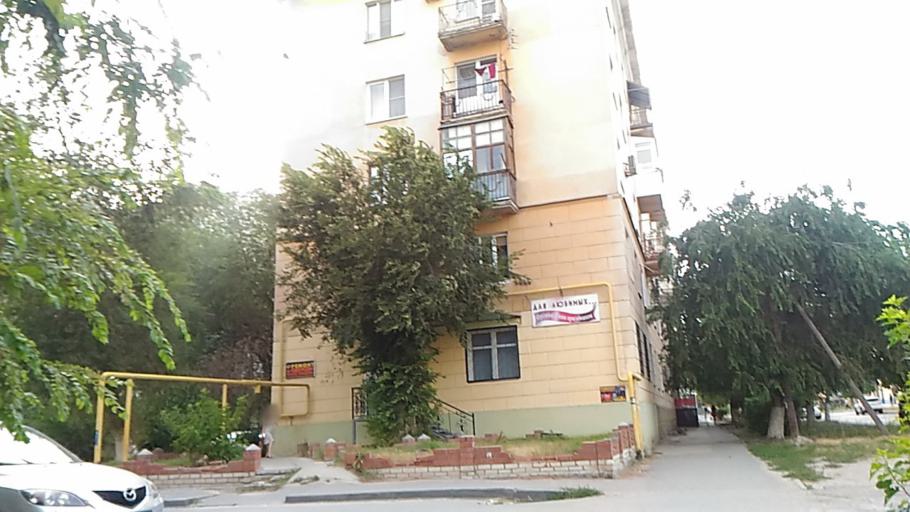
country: RU
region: Volgograd
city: Volgograd
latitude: 48.6966
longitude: 44.4954
